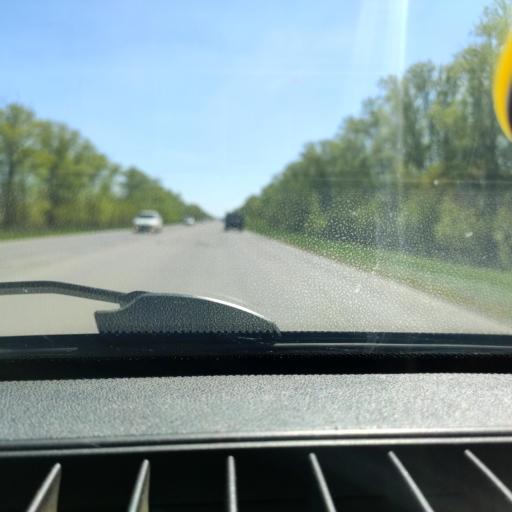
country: RU
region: Samara
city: Tol'yatti
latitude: 53.6032
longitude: 49.4097
